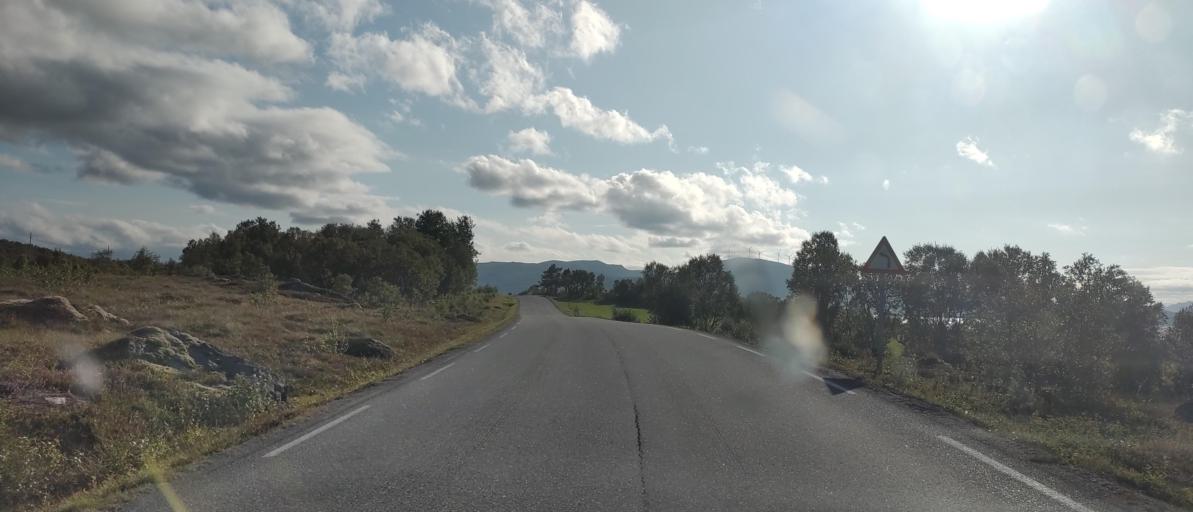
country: NO
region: Nordland
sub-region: Sortland
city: Sortland
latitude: 68.7706
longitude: 15.4706
